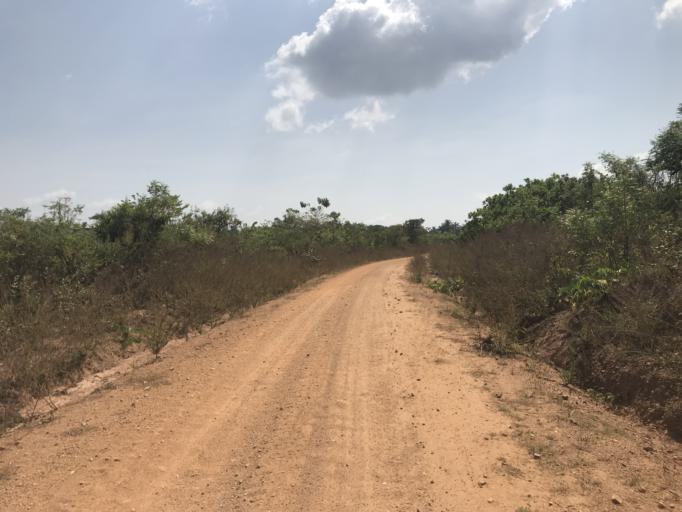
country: NG
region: Osun
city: Ifon
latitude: 7.9871
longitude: 4.5163
